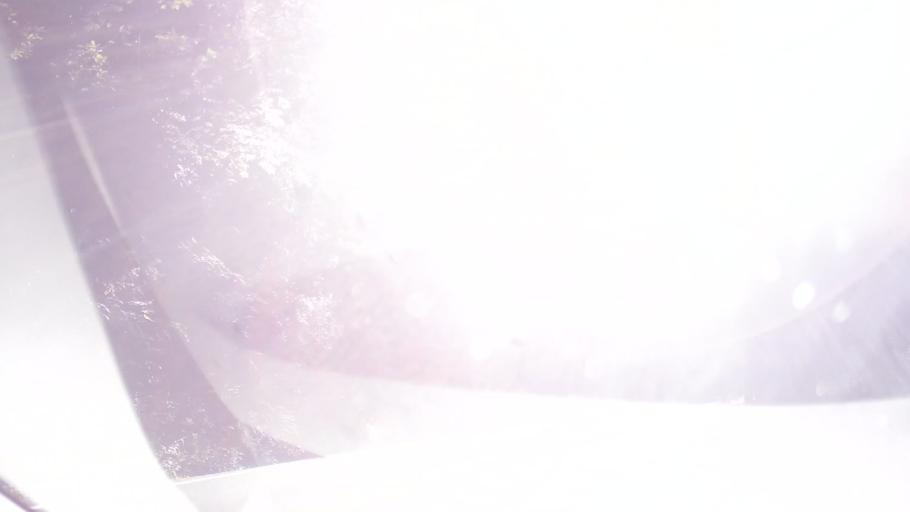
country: US
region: California
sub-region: Mendocino County
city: Brooktrails
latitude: 39.3659
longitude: -123.4990
